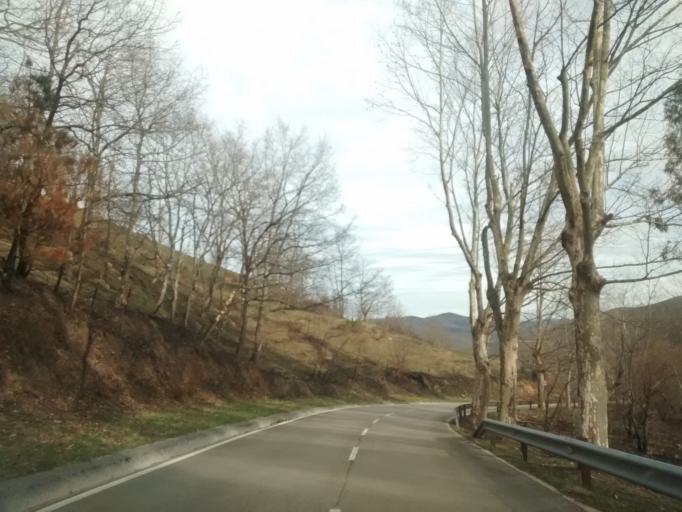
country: ES
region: Cantabria
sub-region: Provincia de Cantabria
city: Ruente
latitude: 43.2319
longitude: -4.3133
